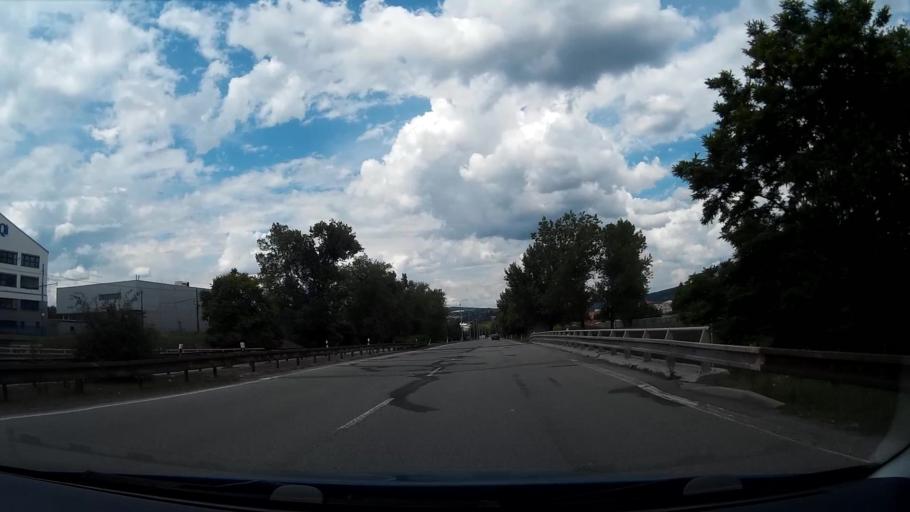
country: CZ
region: South Moravian
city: Troubsko
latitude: 49.2220
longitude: 16.5208
